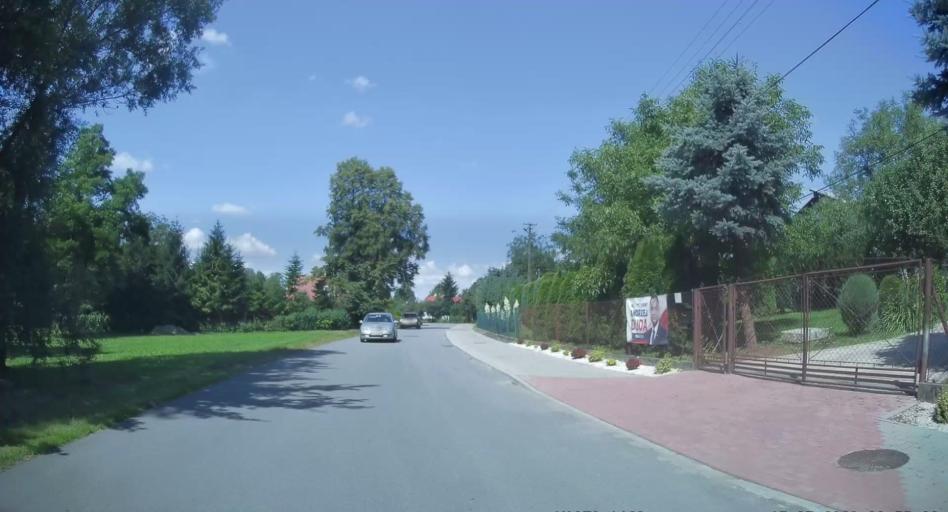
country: PL
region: Subcarpathian Voivodeship
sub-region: Powiat jaroslawski
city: Sosnica
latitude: 49.8648
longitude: 22.8759
